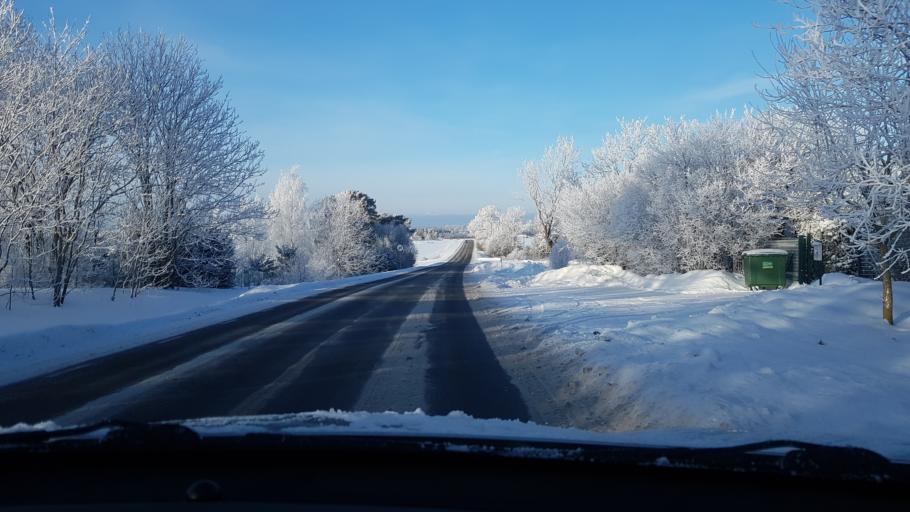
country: EE
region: Harju
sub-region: Saue linn
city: Saue
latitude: 59.3624
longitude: 24.4890
